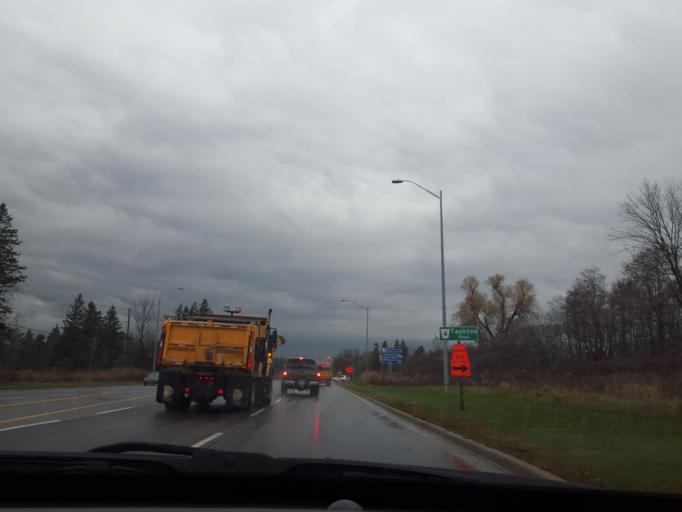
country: CA
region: Ontario
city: Pickering
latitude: 43.8858
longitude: -79.0903
